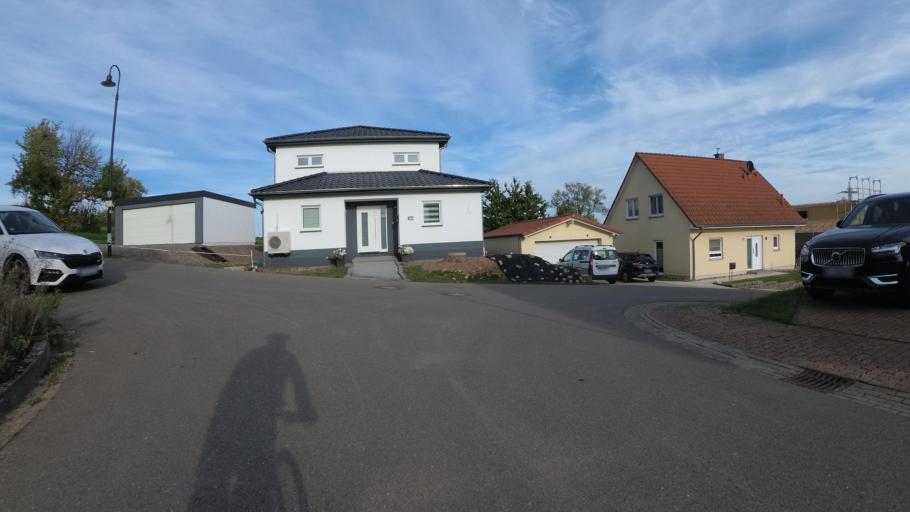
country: DE
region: Rheinland-Pfalz
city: Borsborn
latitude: 49.4441
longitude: 7.4019
